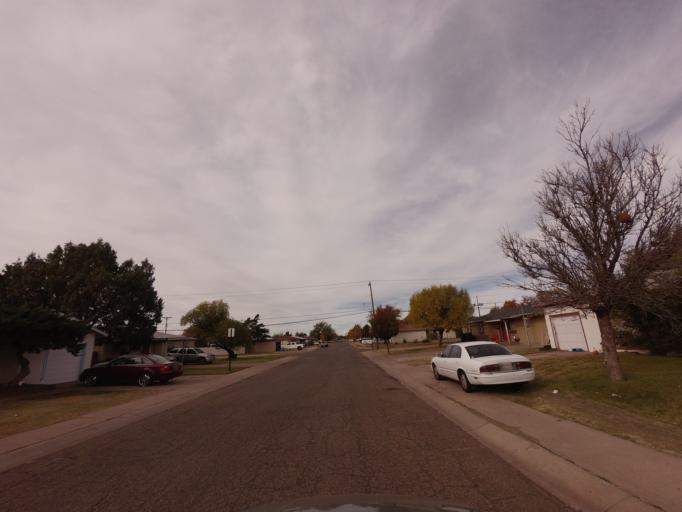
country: US
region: New Mexico
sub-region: Curry County
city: Clovis
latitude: 34.4262
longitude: -103.2136
